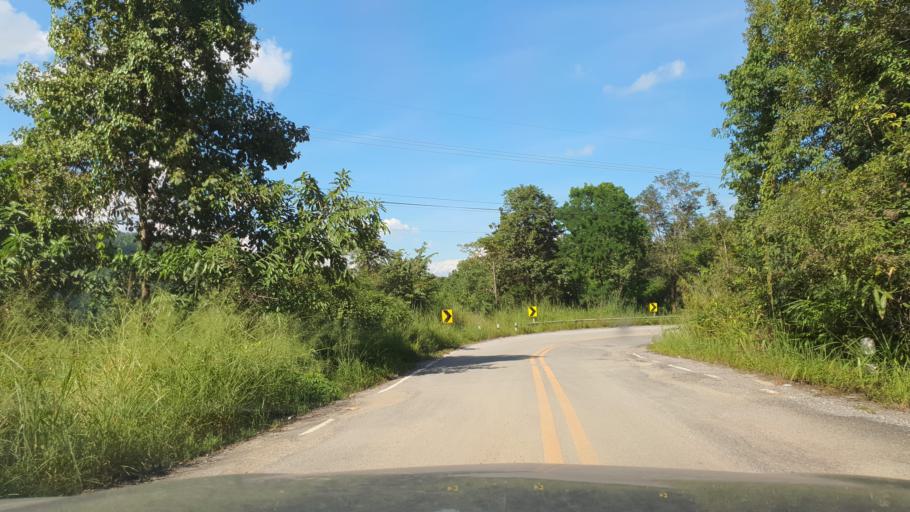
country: TH
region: Chiang Rai
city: Wiang Pa Pao
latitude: 19.3282
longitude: 99.4457
